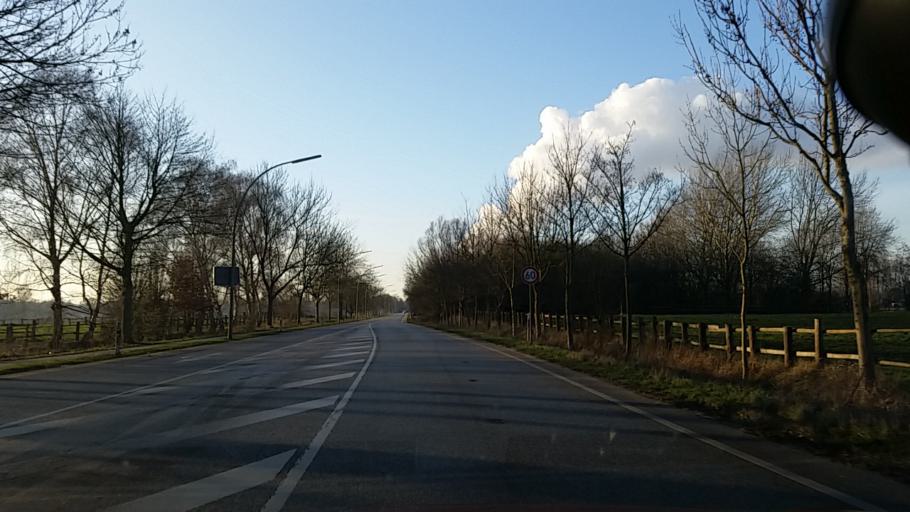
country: DE
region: Hamburg
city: Harburg
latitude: 53.4796
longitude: 10.0180
